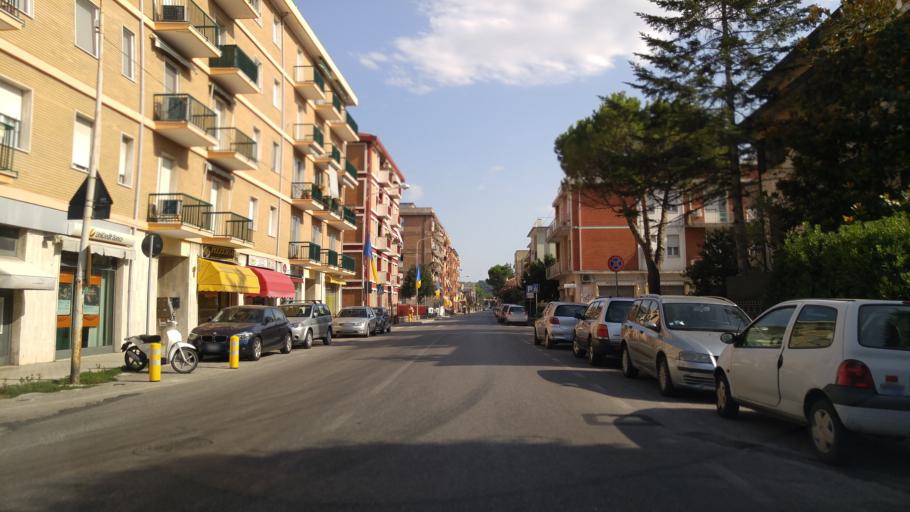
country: IT
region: The Marches
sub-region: Provincia di Pesaro e Urbino
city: Pesaro
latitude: 43.9000
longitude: 12.9197
